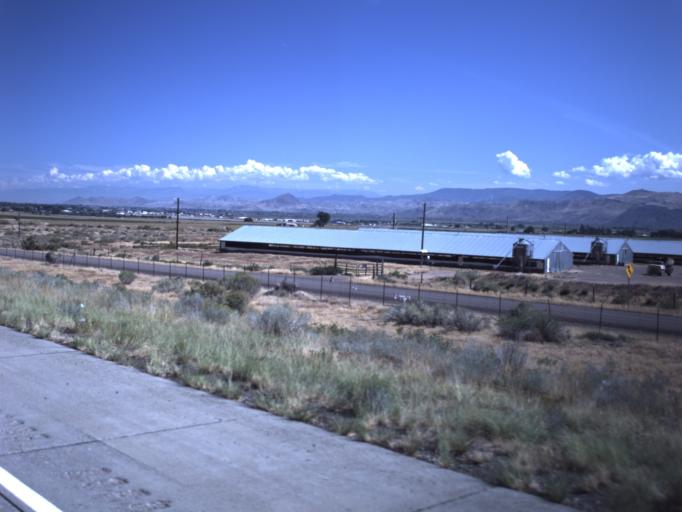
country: US
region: Utah
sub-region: Sevier County
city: Richfield
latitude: 38.7164
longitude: -112.1341
